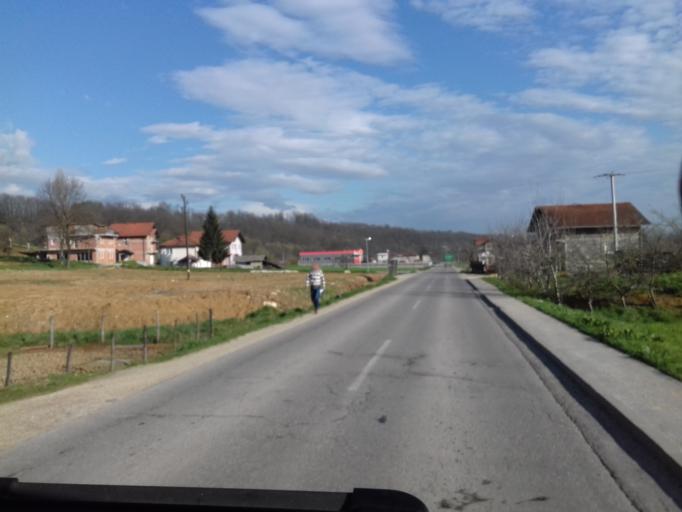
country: BA
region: Federation of Bosnia and Herzegovina
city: Tesanjka
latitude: 44.6472
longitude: 18.0184
